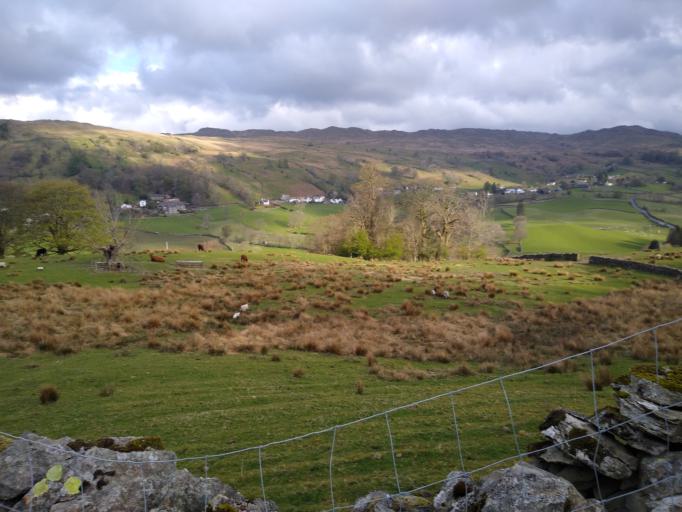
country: GB
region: England
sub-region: Cumbria
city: Windermere
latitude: 54.4144
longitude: -2.9038
